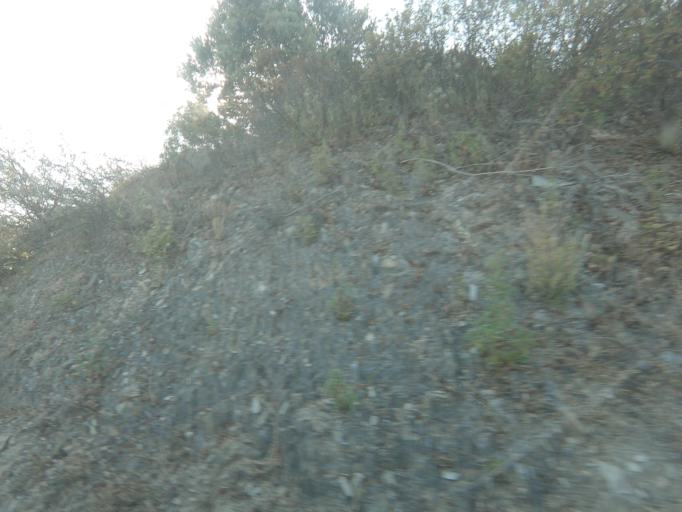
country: PT
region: Vila Real
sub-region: Sabrosa
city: Vilela
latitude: 41.1714
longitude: -7.5905
